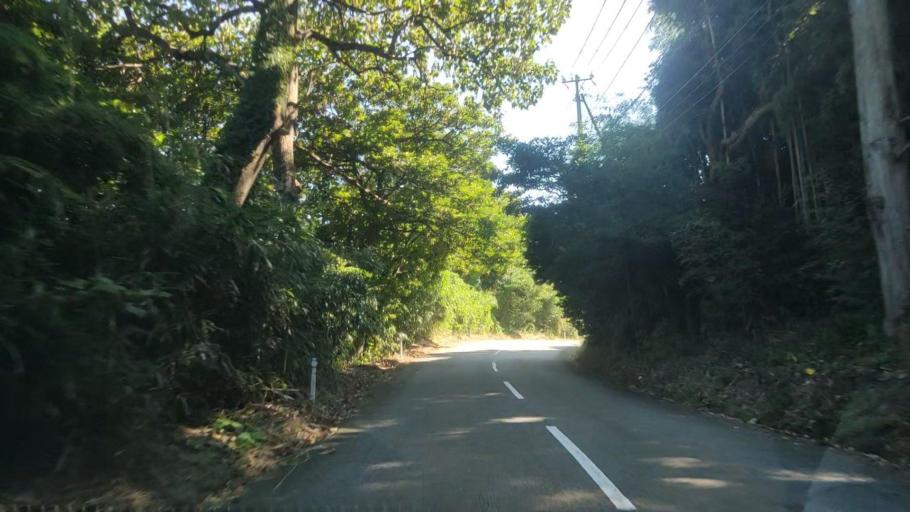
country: JP
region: Ishikawa
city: Nanao
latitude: 37.5206
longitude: 137.3268
